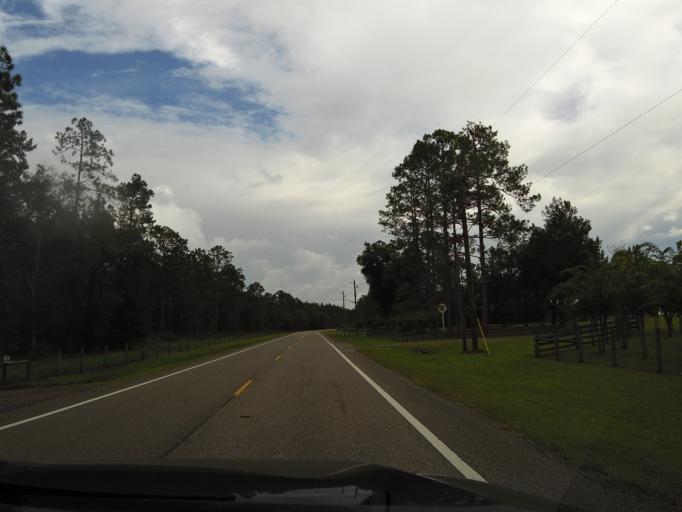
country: US
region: Florida
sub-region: Duval County
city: Baldwin
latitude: 30.3617
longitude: -81.9186
